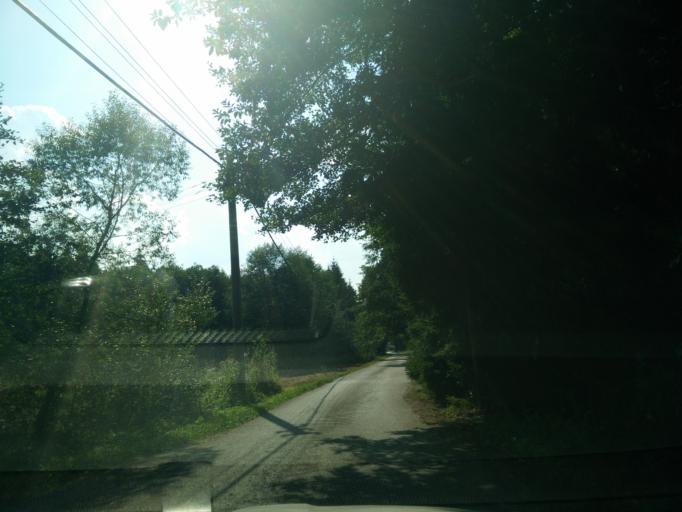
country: SK
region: Zilinsky
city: Rajec
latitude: 49.1026
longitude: 18.7175
